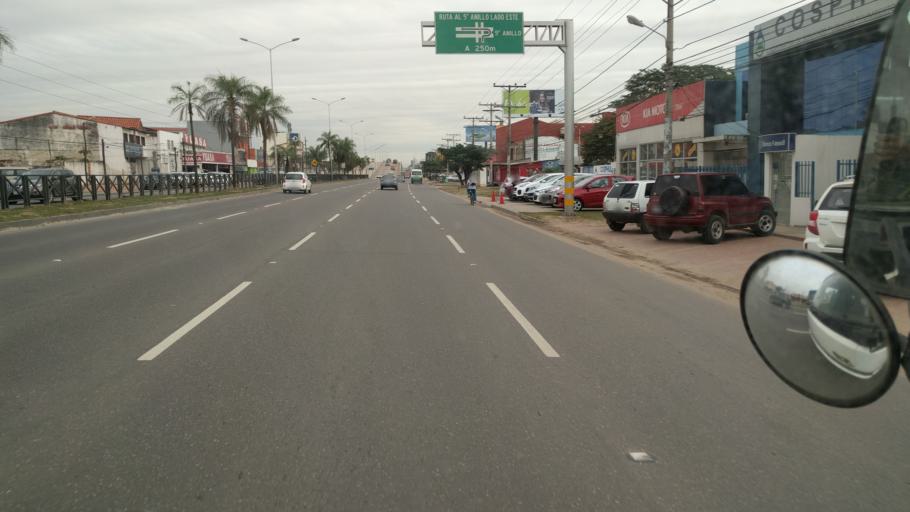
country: BO
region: Santa Cruz
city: Santa Cruz de la Sierra
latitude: -17.7373
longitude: -63.1704
